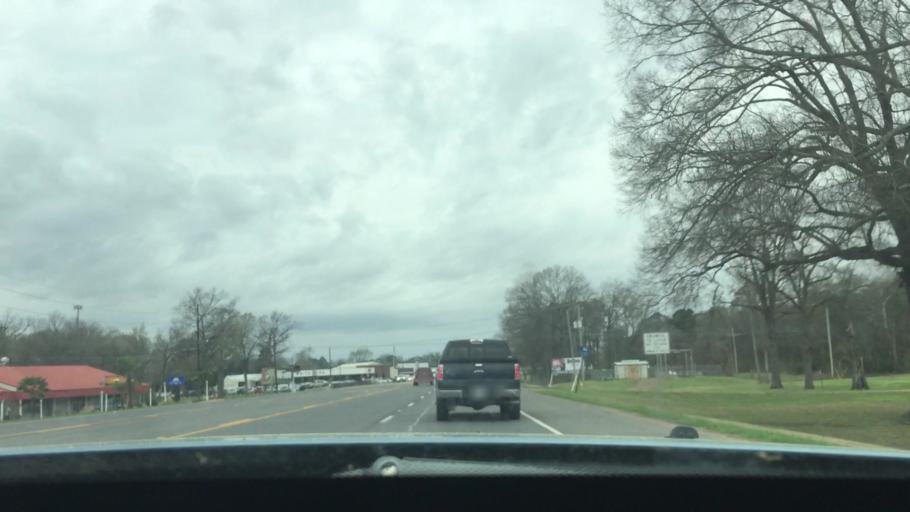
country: US
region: Louisiana
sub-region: Franklin Parish
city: Winnsboro
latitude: 32.1540
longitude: -91.7101
